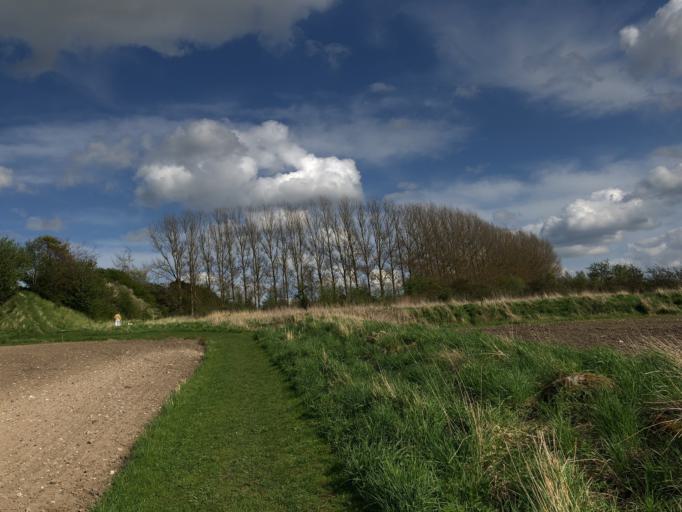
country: DK
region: Zealand
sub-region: Ringsted Kommune
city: Ringsted
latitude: 55.4285
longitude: 11.7776
